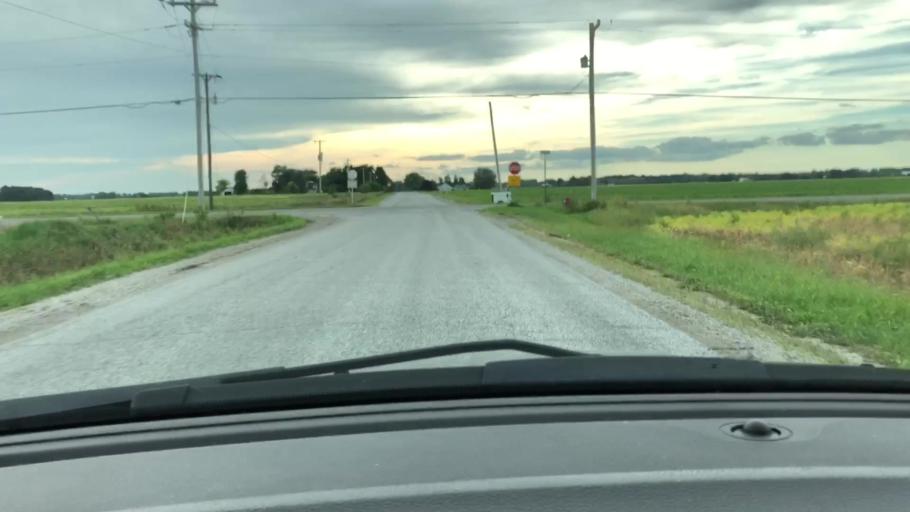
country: US
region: Michigan
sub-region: Saginaw County
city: Carrollton
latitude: 43.5092
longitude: -84.0102
